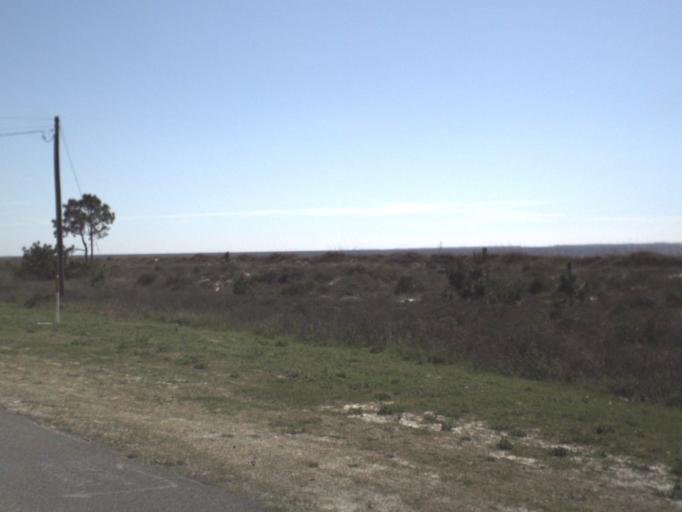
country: US
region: Florida
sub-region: Bay County
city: Mexico Beach
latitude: 29.8926
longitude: -85.3584
